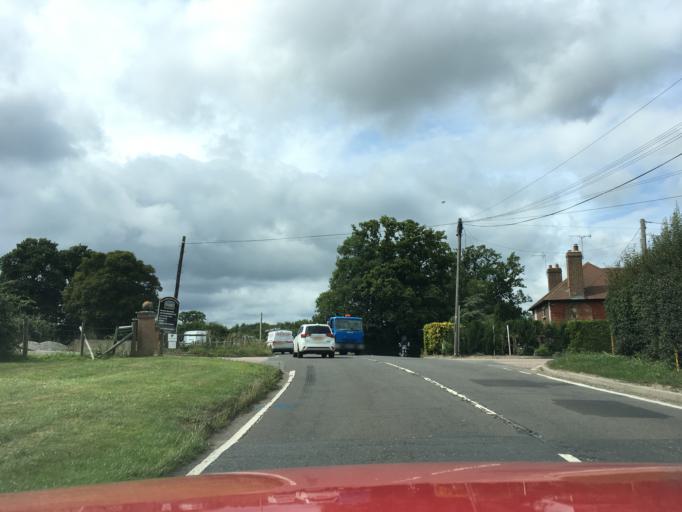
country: GB
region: England
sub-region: Kent
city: Marden
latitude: 51.1111
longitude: 0.4317
